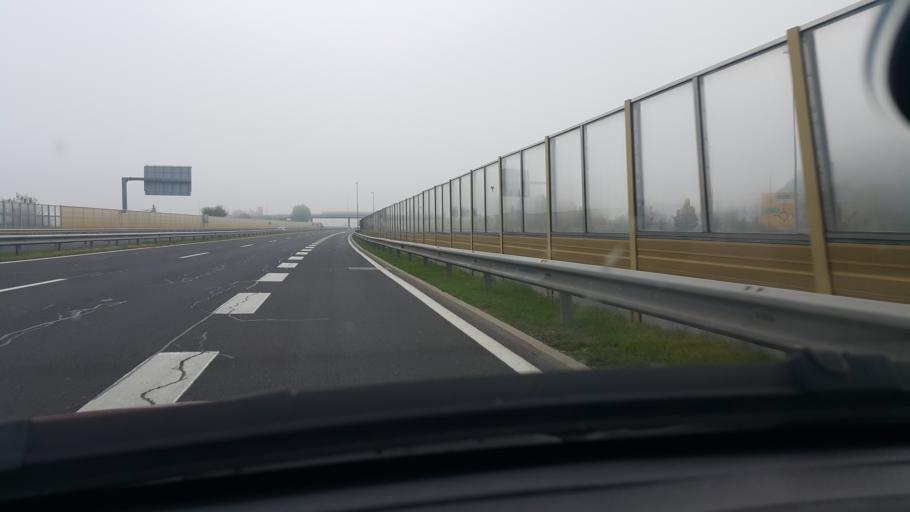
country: SI
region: Brezice
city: Brezice
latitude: 45.8909
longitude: 15.6068
